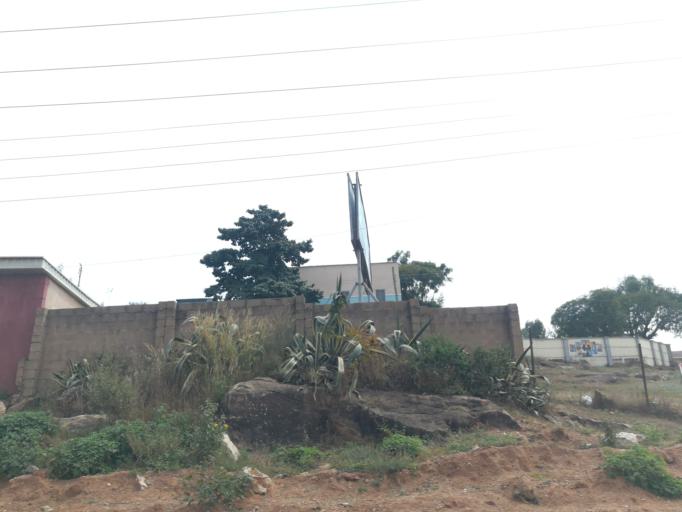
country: NG
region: Plateau
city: Jos
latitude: 9.8936
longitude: 8.8647
